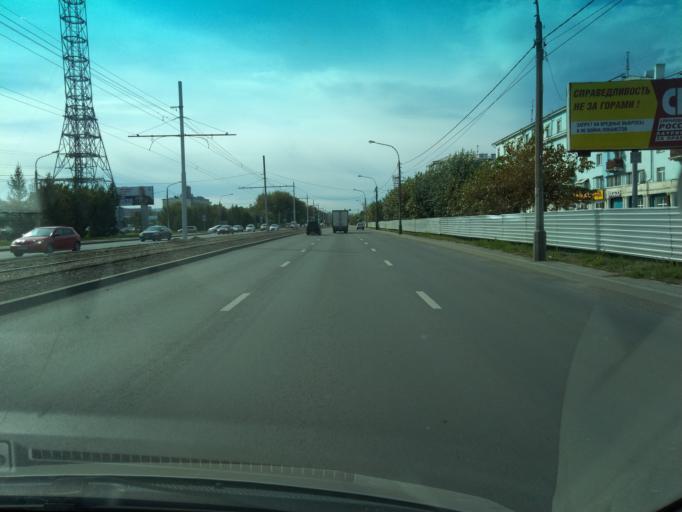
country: RU
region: Krasnoyarskiy
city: Berezovka
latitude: 56.0218
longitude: 93.0097
